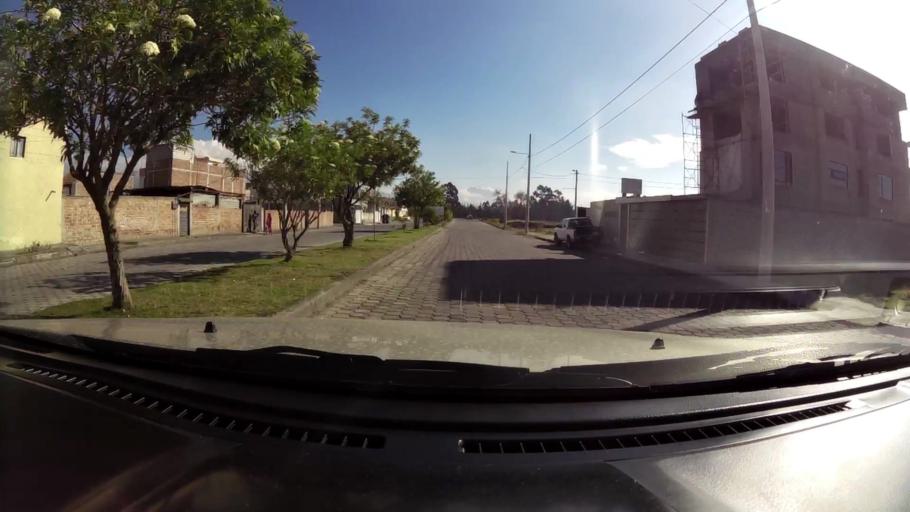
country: EC
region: Chimborazo
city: Riobamba
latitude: -1.6485
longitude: -78.6640
